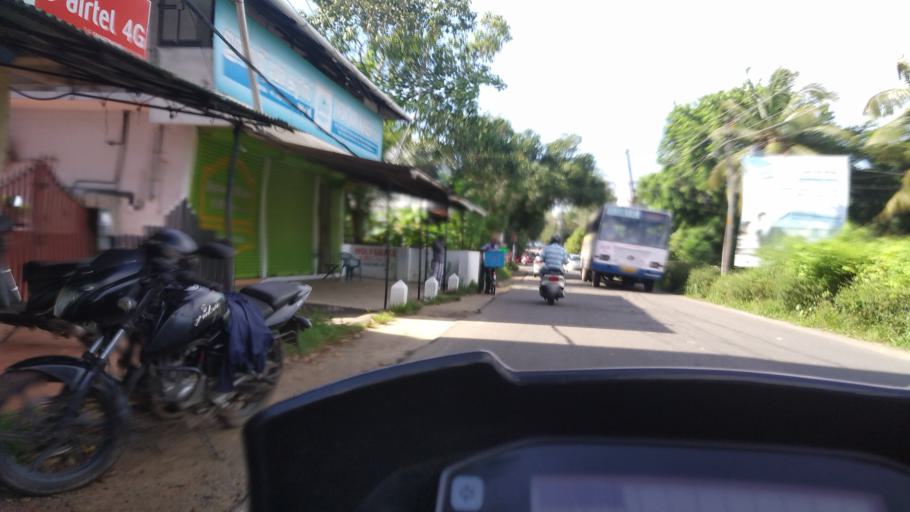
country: IN
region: Kerala
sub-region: Ernakulam
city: Elur
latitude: 10.0613
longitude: 76.2137
